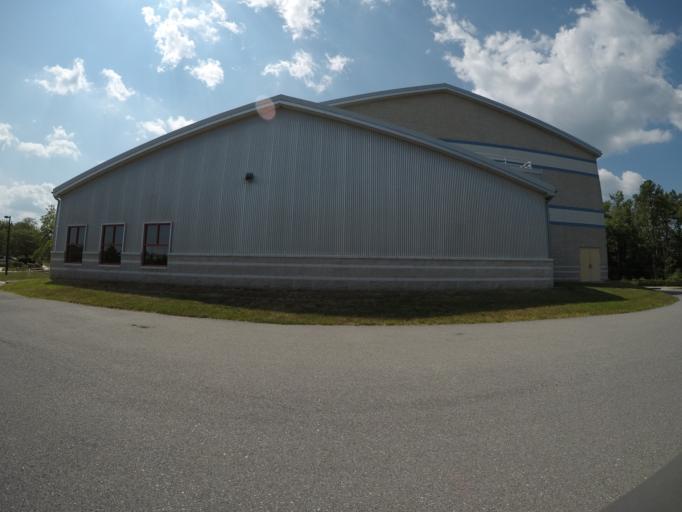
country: US
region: Maryland
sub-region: Harford County
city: Edgewood
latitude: 39.4337
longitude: -76.3093
